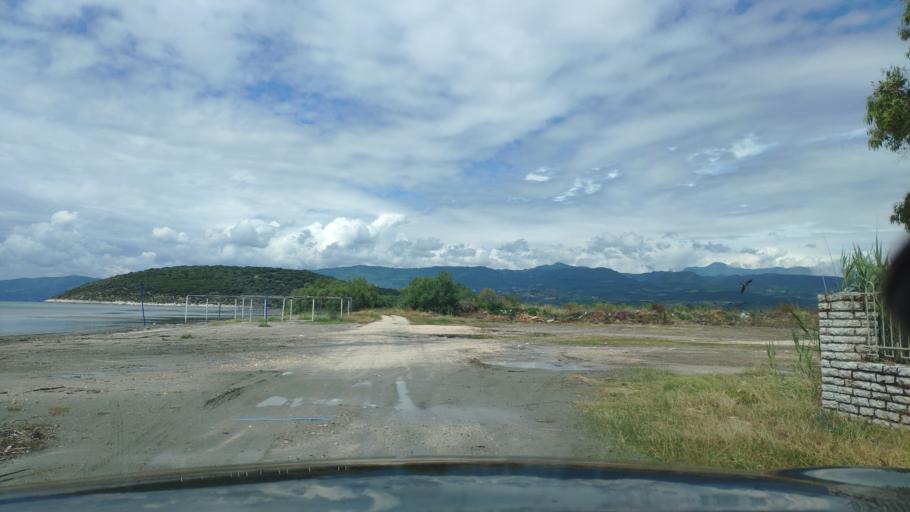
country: GR
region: West Greece
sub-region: Nomos Aitolias kai Akarnanias
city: Krikellos
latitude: 38.9315
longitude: 21.1421
